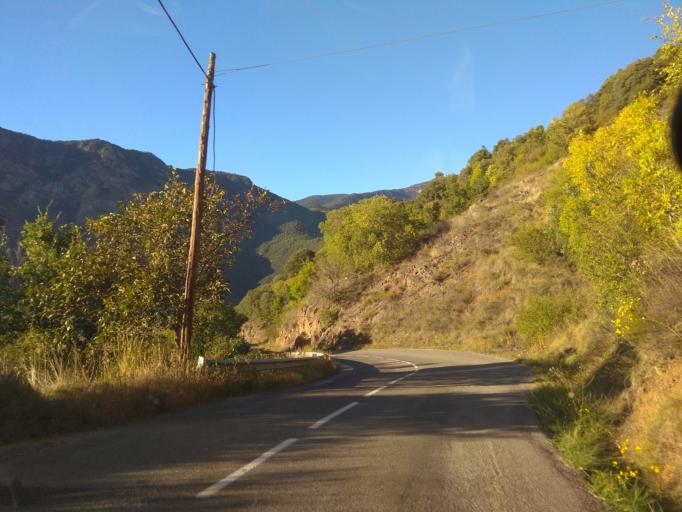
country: ES
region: Catalonia
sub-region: Provincia de Lleida
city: el Pont de Bar
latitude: 42.3522
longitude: 1.5829
